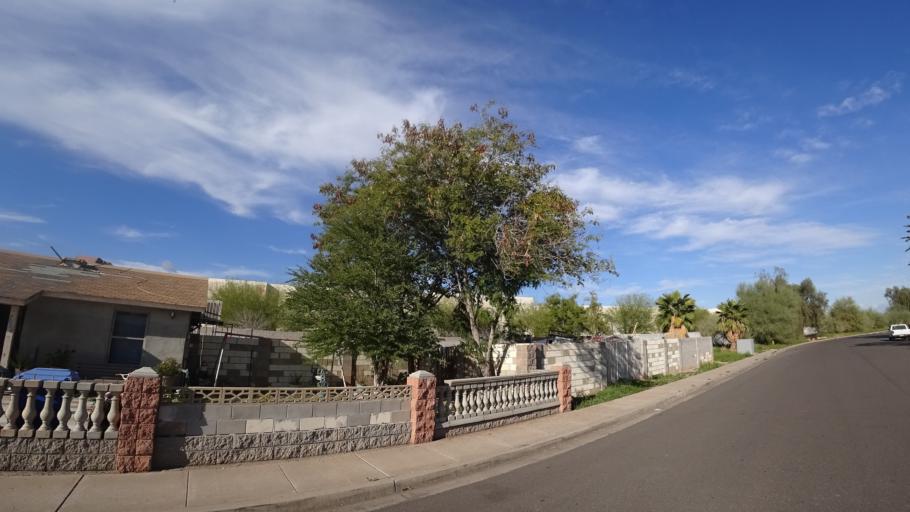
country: US
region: Arizona
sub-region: Maricopa County
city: Tolleson
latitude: 33.4585
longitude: -112.2107
